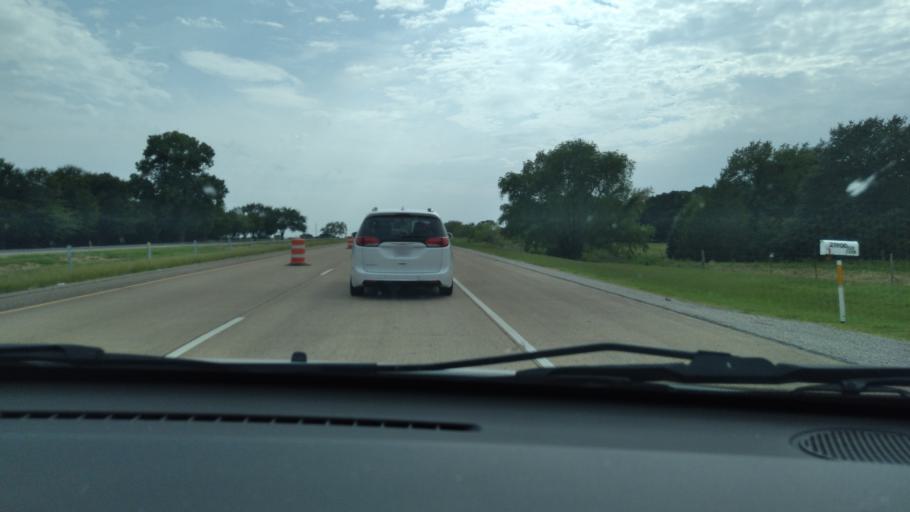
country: US
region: Texas
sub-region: Hill County
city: Hubbard
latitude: 31.8839
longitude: -96.7470
